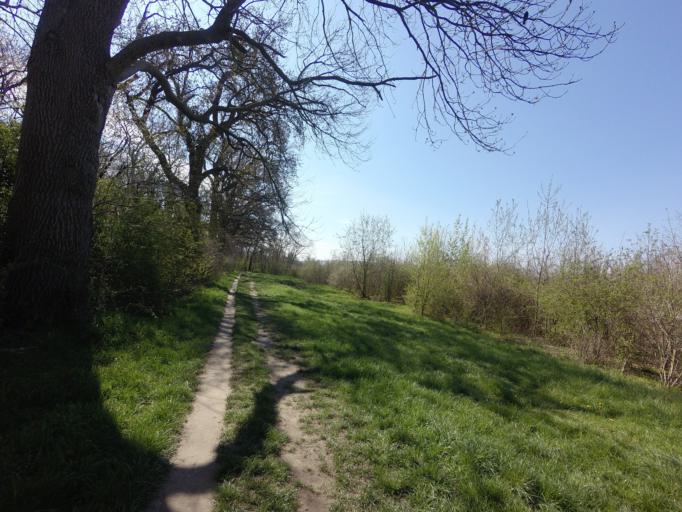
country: NL
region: Limburg
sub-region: Gemeente Maastricht
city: Maastricht
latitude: 50.8195
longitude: 5.6632
